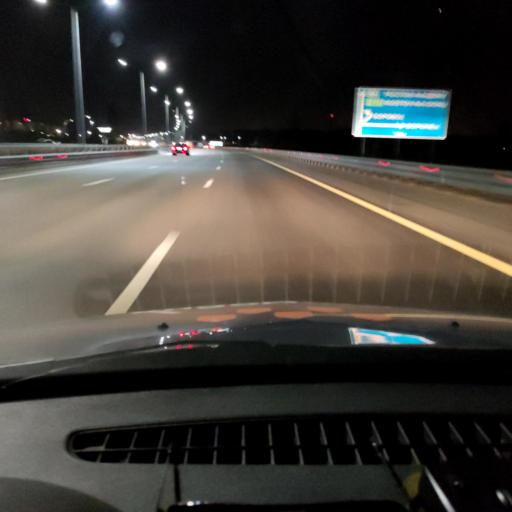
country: RU
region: Voronezj
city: Somovo
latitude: 51.7493
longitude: 39.3055
